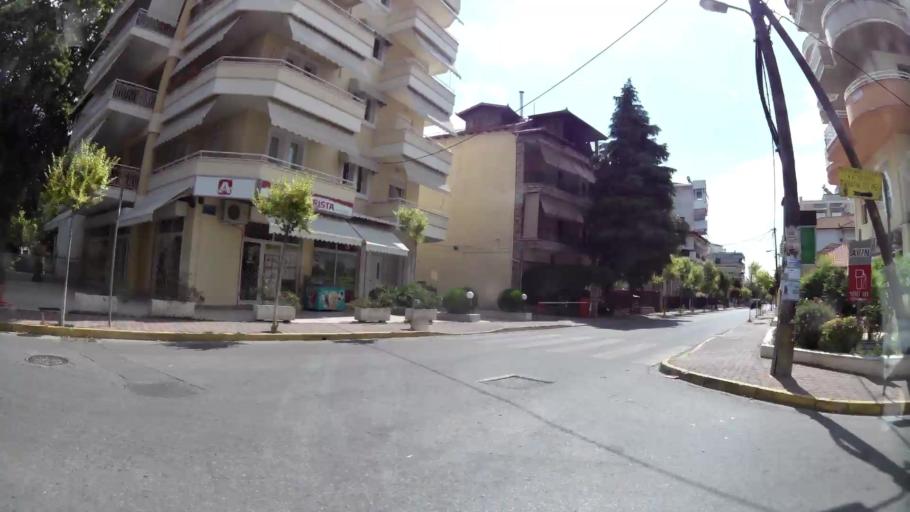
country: GR
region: Central Macedonia
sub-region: Nomos Pierias
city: Katerini
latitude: 40.2694
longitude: 22.4988
